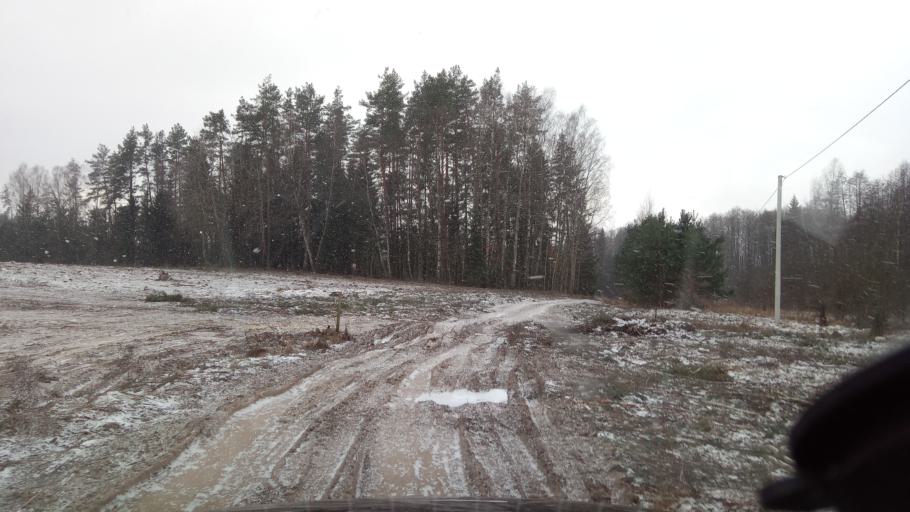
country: LT
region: Alytaus apskritis
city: Varena
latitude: 54.1279
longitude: 24.6780
